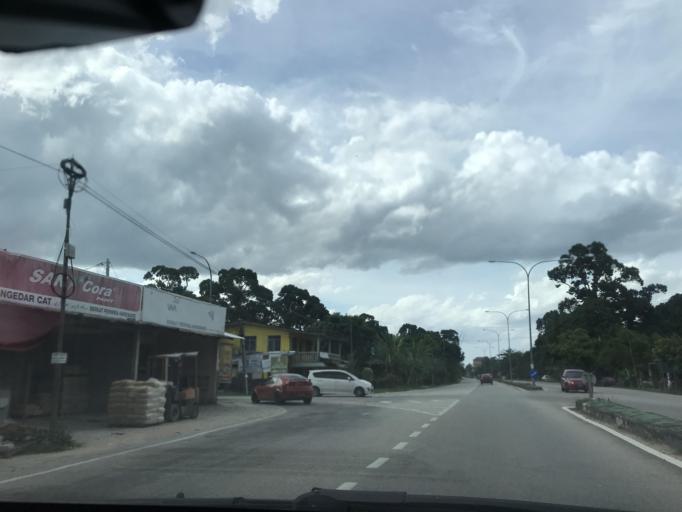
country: MY
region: Kelantan
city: Kampong Pangkal Kalong
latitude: 5.9189
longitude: 102.1887
